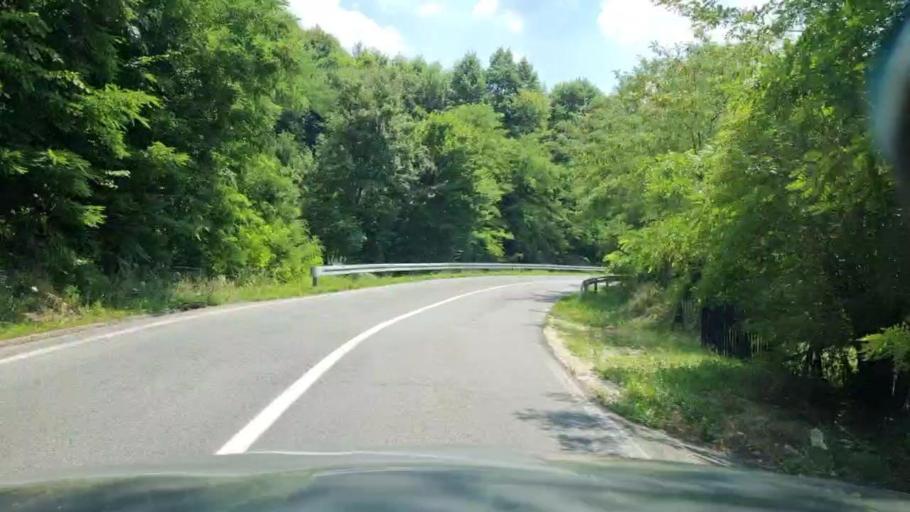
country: BA
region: Federation of Bosnia and Herzegovina
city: Tojsici
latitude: 44.5351
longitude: 18.8364
